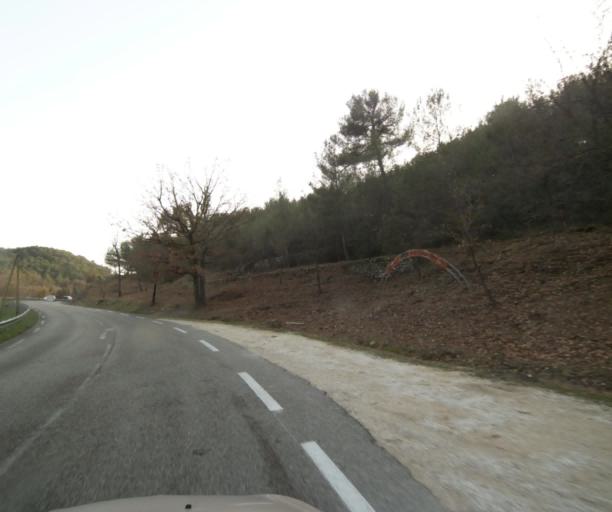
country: FR
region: Provence-Alpes-Cote d'Azur
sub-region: Departement des Bouches-du-Rhone
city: Rognes
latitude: 43.6701
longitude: 5.3527
